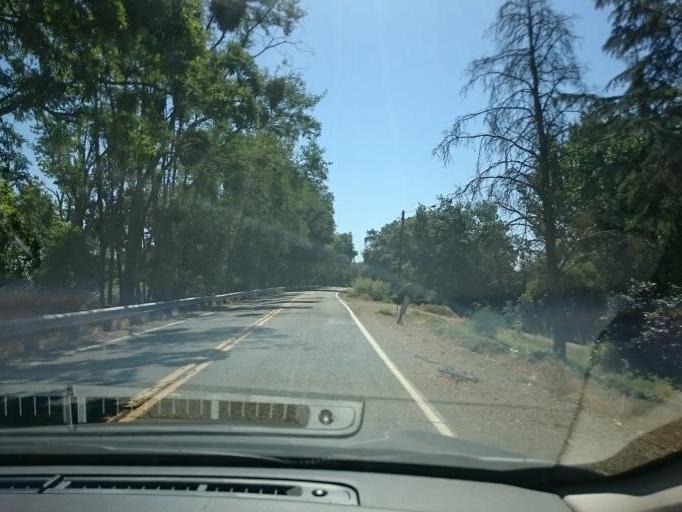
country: US
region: California
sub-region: Sacramento County
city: Parkway
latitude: 38.4722
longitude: -121.5121
